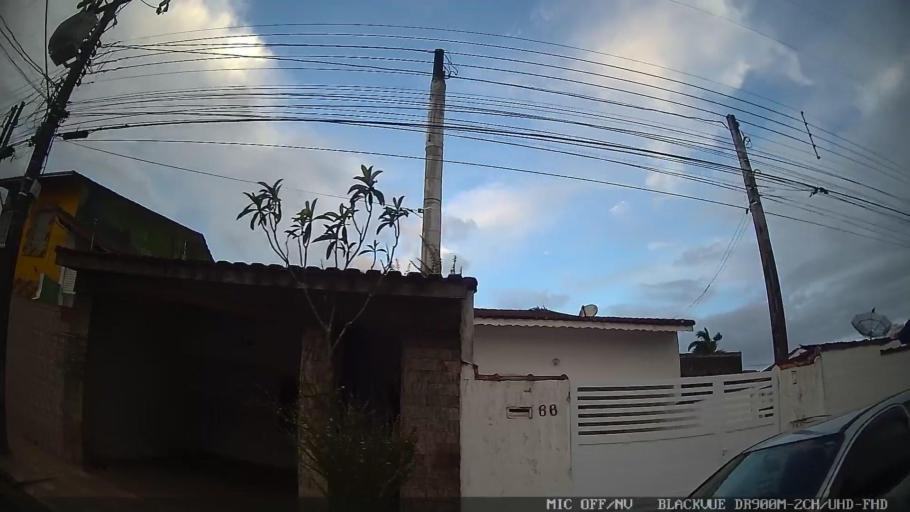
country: BR
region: Sao Paulo
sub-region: Itanhaem
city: Itanhaem
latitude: -24.1764
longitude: -46.7864
